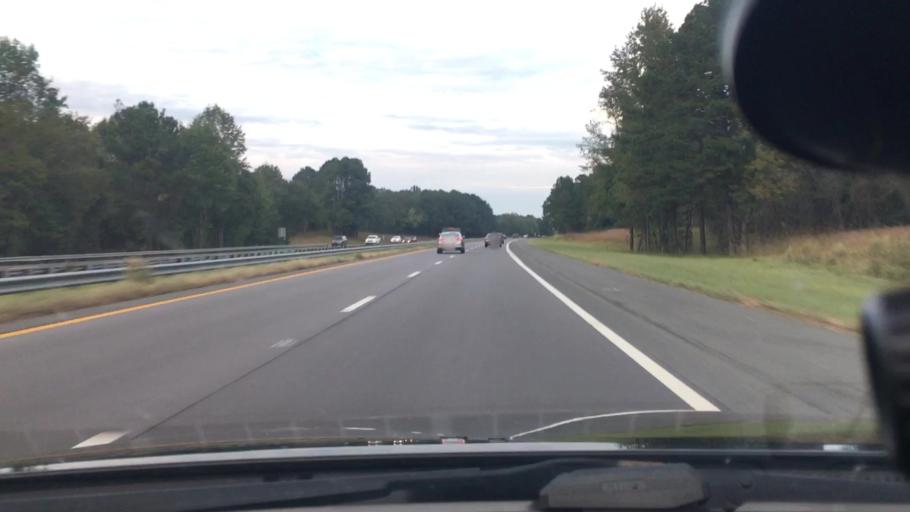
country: US
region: North Carolina
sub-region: Chatham County
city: Farmville
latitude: 35.6061
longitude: -79.1075
